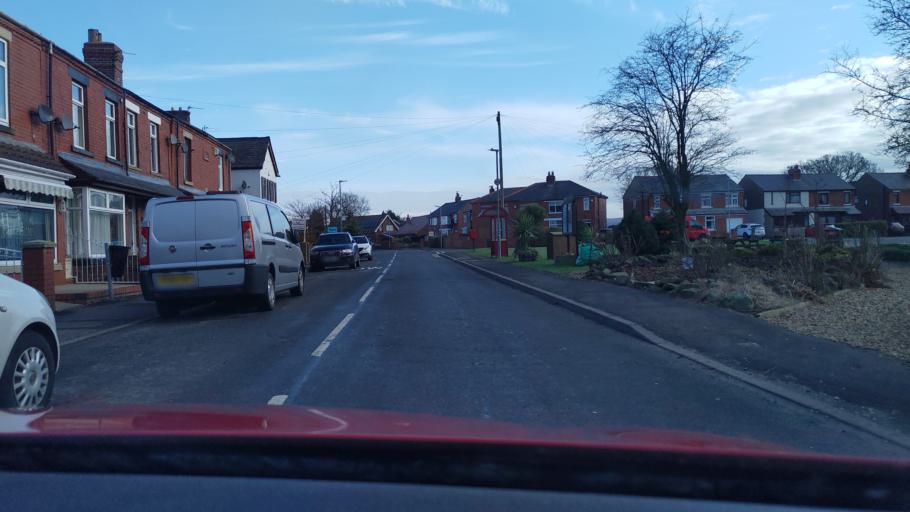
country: GB
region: England
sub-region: Lancashire
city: Coppull
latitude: 53.6247
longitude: -2.6531
